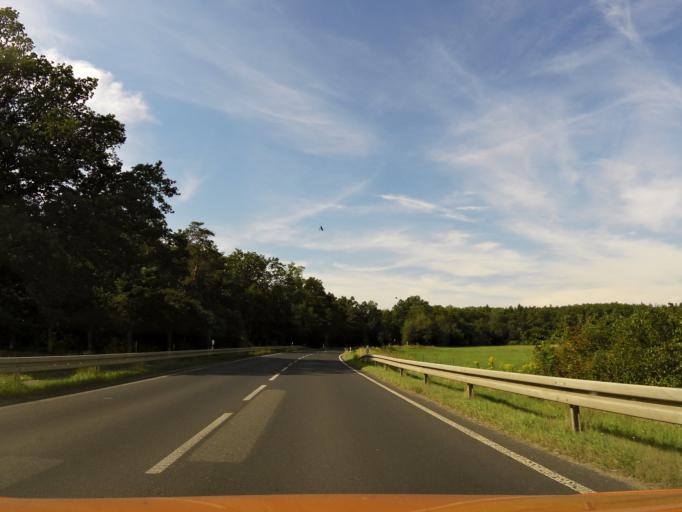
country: DE
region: Brandenburg
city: Teltow
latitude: 52.3622
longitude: 13.2681
